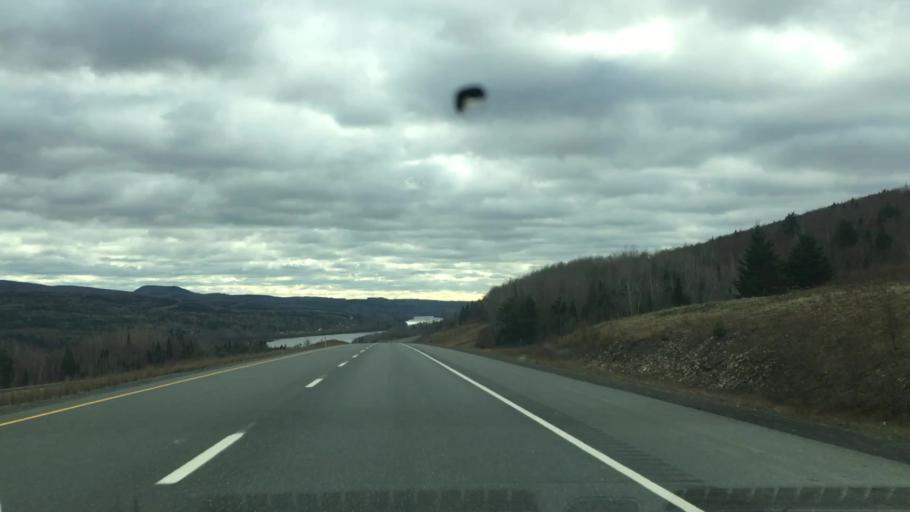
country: US
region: Maine
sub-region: Aroostook County
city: Fort Fairfield
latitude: 46.6915
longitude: -67.7381
